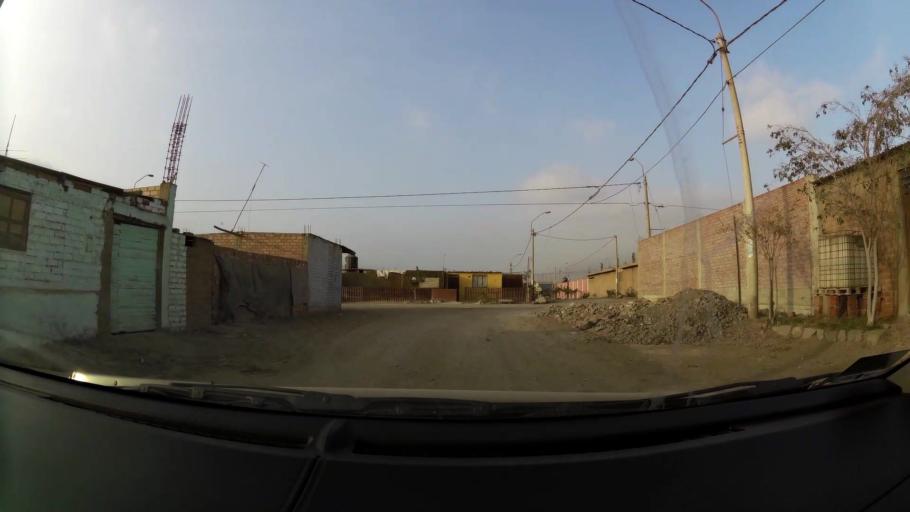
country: PE
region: Lima
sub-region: Lima
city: Santa Rosa
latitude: -11.7473
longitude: -77.1477
